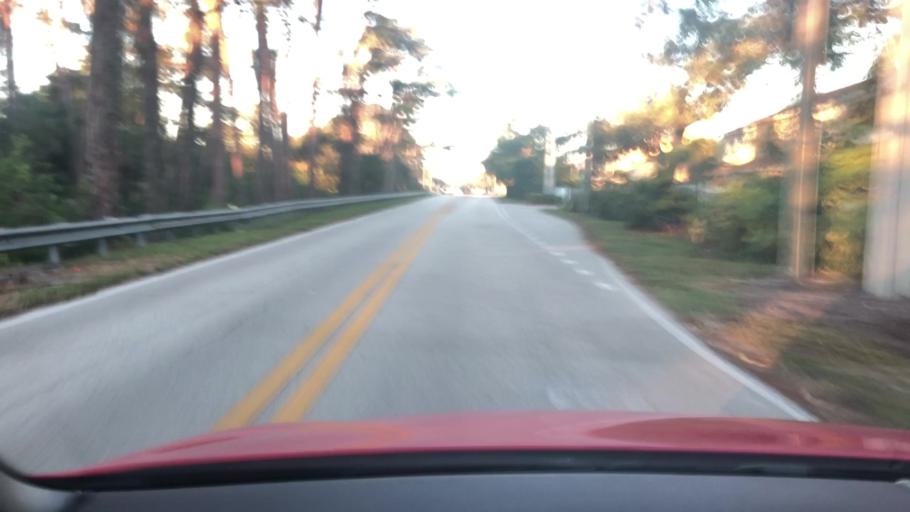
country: US
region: Florida
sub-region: Volusia County
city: South Daytona
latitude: 29.1586
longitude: -80.9981
